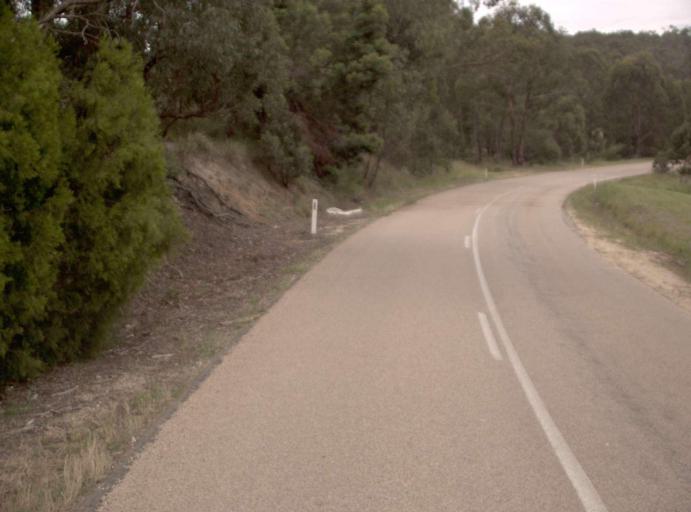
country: AU
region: Victoria
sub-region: East Gippsland
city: Bairnsdale
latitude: -37.7541
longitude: 147.5980
